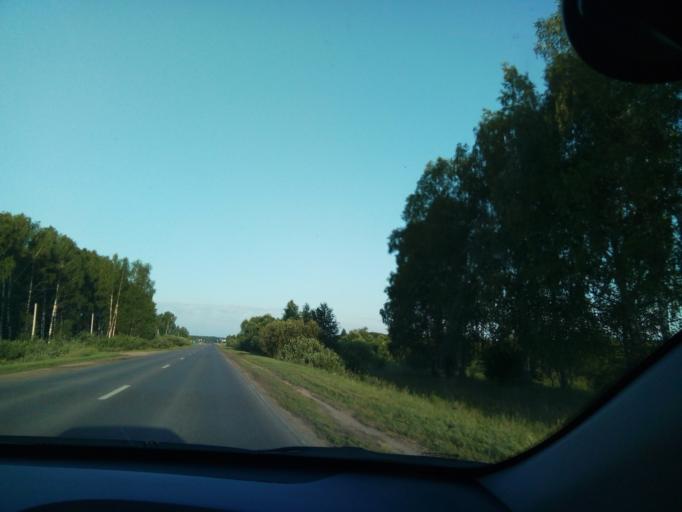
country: RU
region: Nizjnij Novgorod
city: Satis
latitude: 54.9379
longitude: 43.2437
